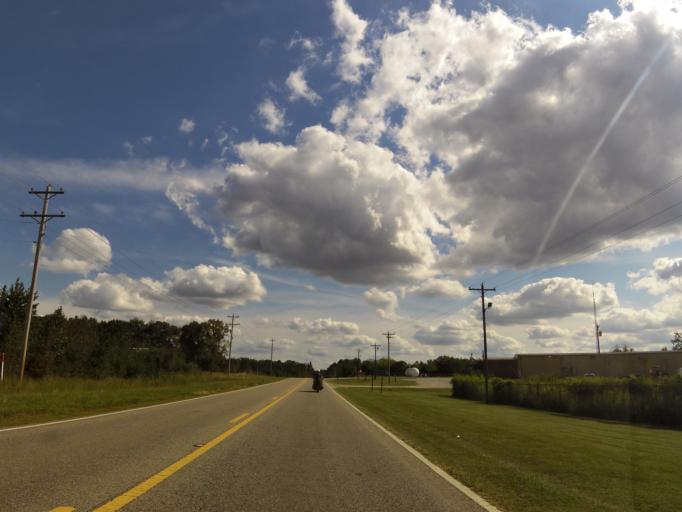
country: US
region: Alabama
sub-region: Dallas County
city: Selmont-West Selmont
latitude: 32.3105
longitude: -86.9855
